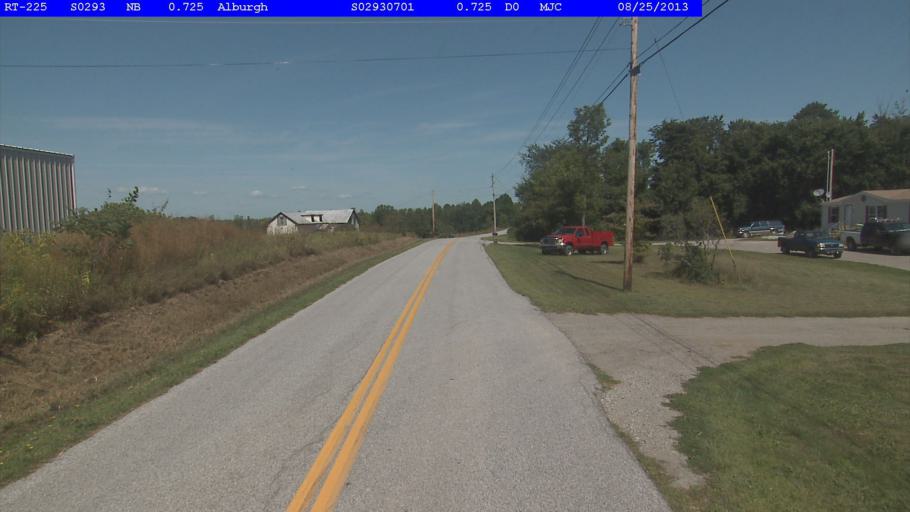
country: US
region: New York
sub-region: Clinton County
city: Rouses Point
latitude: 44.9991
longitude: -73.2962
